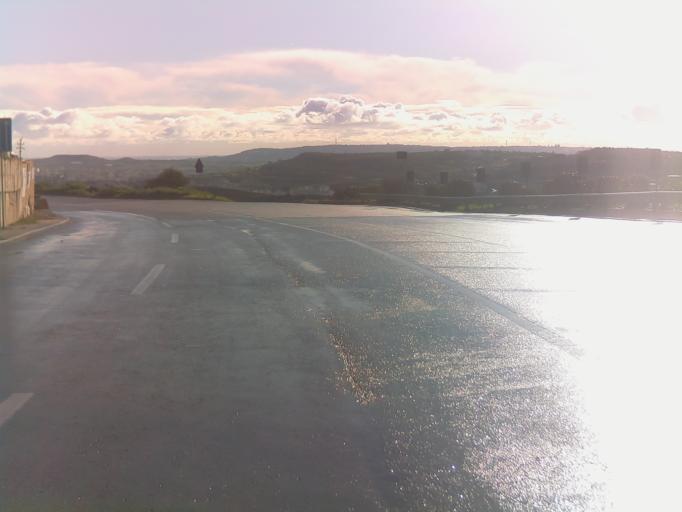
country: MT
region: Il-Mellieha
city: Mellieha
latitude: 35.9528
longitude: 14.3653
